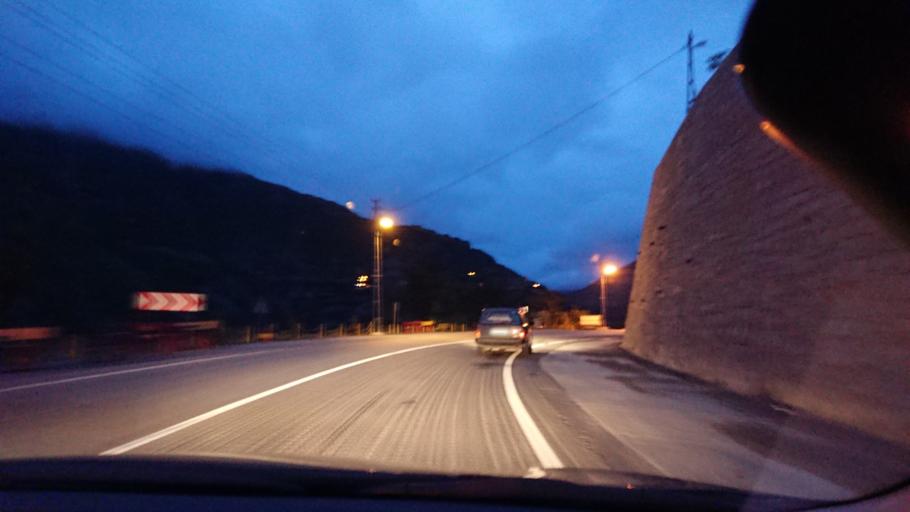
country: TR
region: Gumushane
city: Kurtun
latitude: 40.6722
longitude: 39.1387
